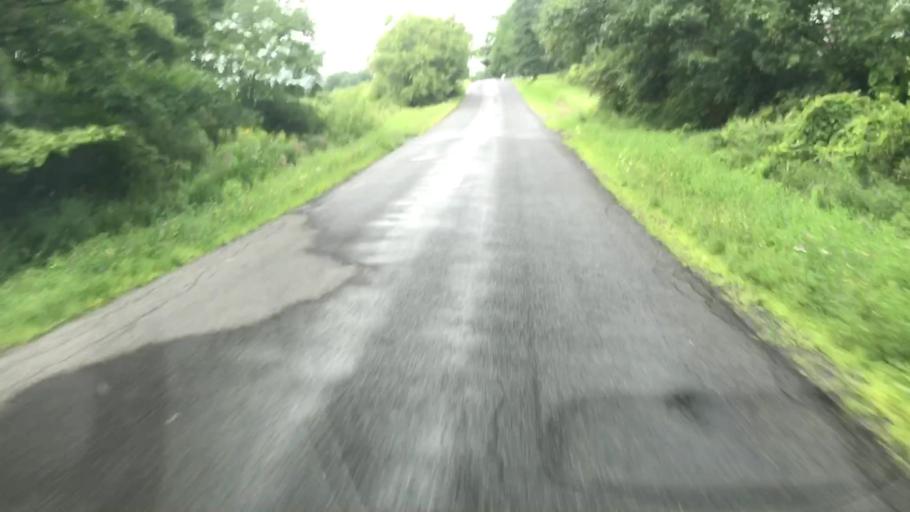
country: US
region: New York
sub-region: Cayuga County
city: Melrose Park
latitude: 42.9630
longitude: -76.5071
